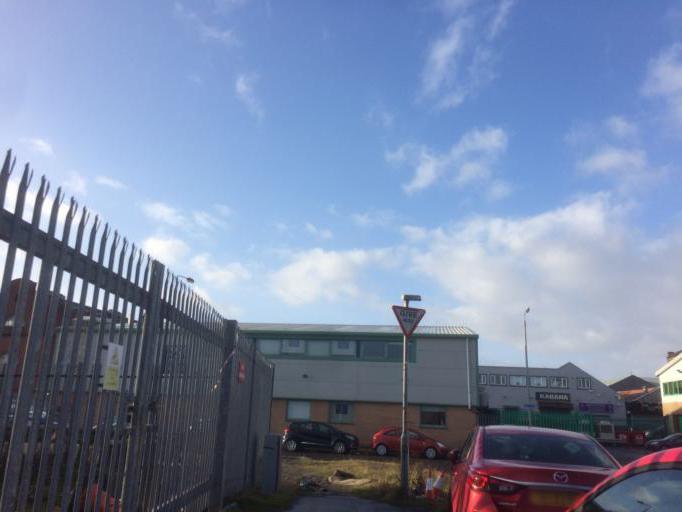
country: GB
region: Scotland
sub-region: Glasgow City
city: Glasgow
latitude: 55.8521
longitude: -4.2763
